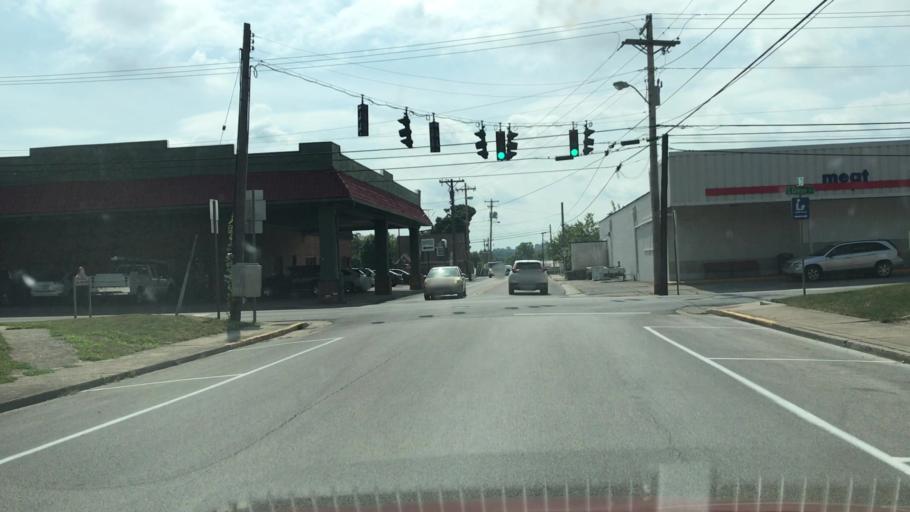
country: US
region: Kentucky
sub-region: Barren County
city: Glasgow
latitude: 36.9935
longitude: -85.9139
